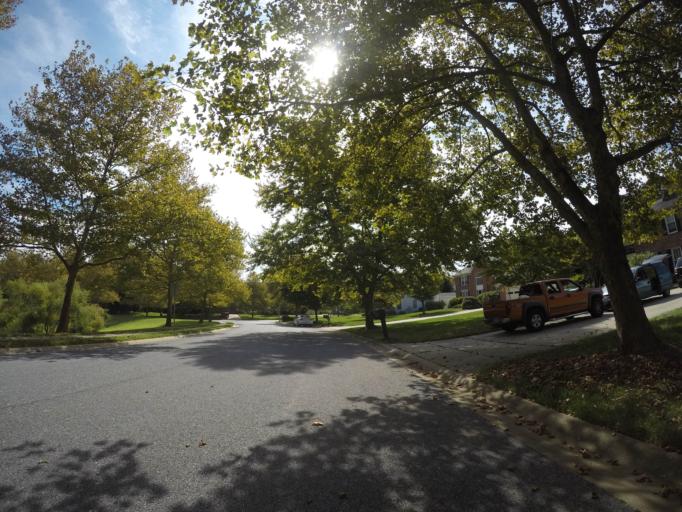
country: US
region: Maryland
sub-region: Howard County
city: Columbia
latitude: 39.2638
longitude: -76.8725
